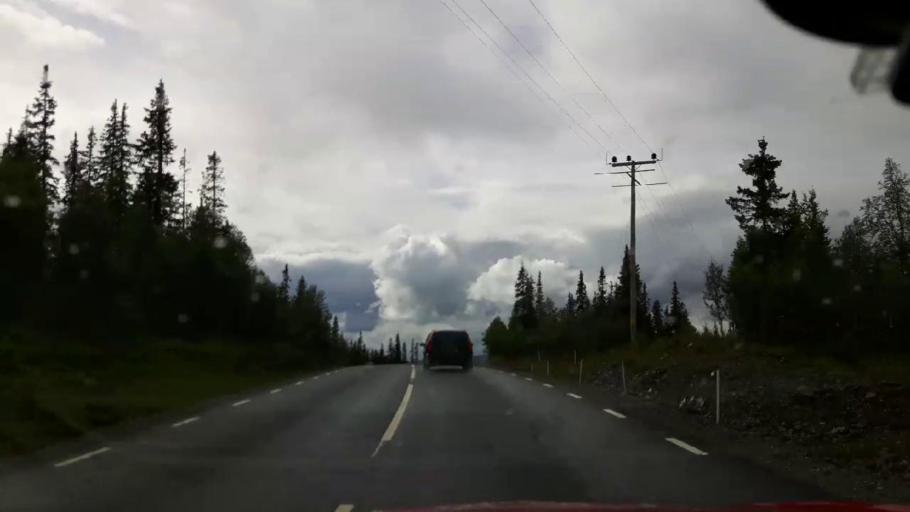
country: NO
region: Nord-Trondelag
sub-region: Royrvik
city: Royrvik
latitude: 64.8468
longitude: 14.1715
